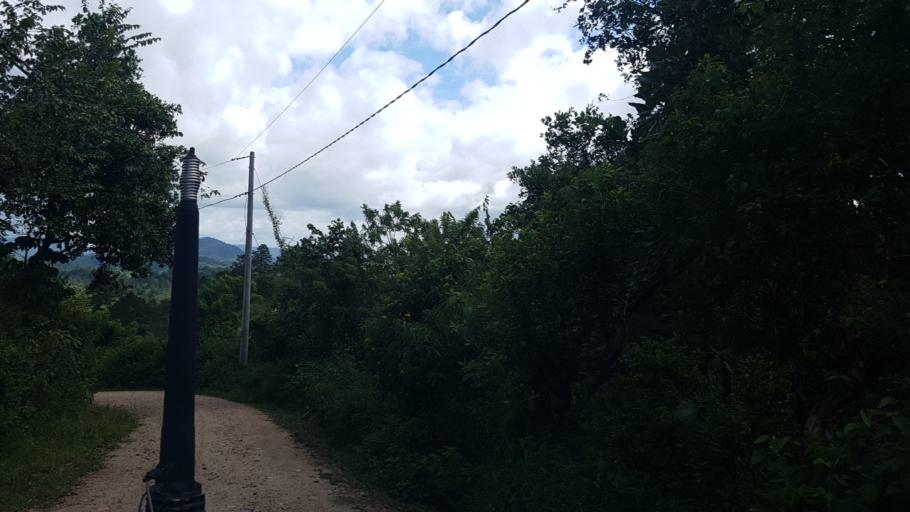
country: NI
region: Nueva Segovia
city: Ciudad Antigua
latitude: 13.6531
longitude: -86.2460
